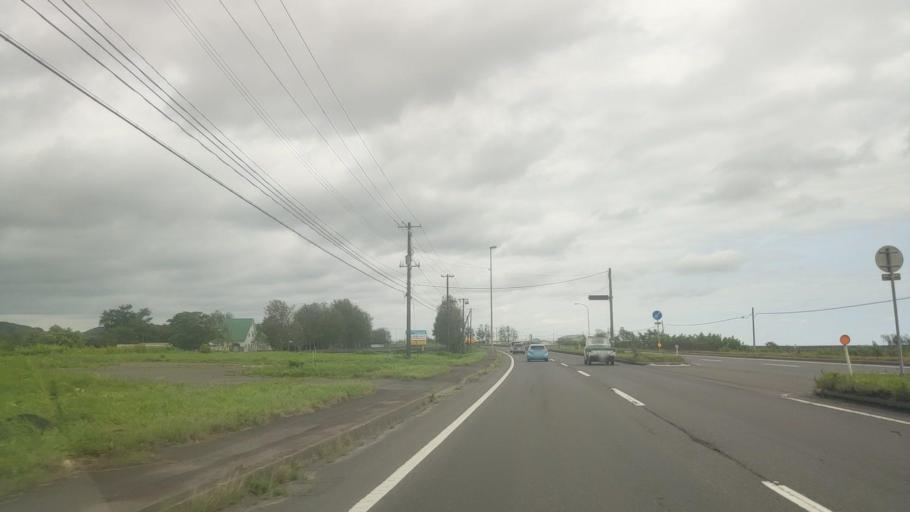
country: JP
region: Hokkaido
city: Shiraoi
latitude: 42.5664
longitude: 141.3896
